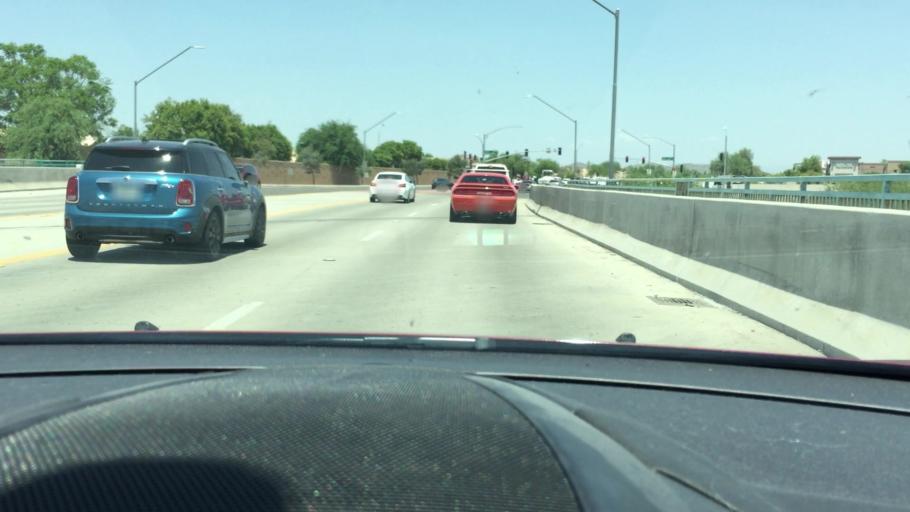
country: US
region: Arizona
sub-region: Maricopa County
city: Sun City
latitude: 33.6511
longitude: -112.2373
